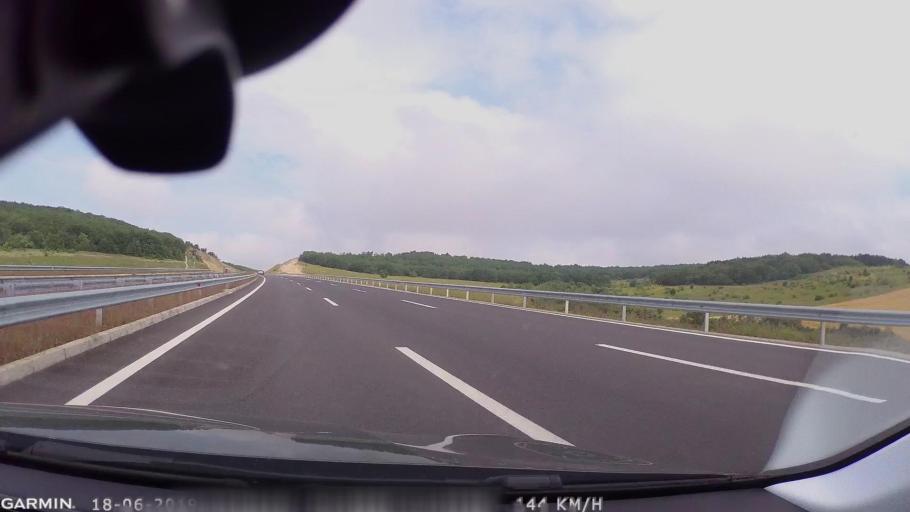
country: MK
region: Sveti Nikole
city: Gorobinci
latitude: 41.9193
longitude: 21.8718
